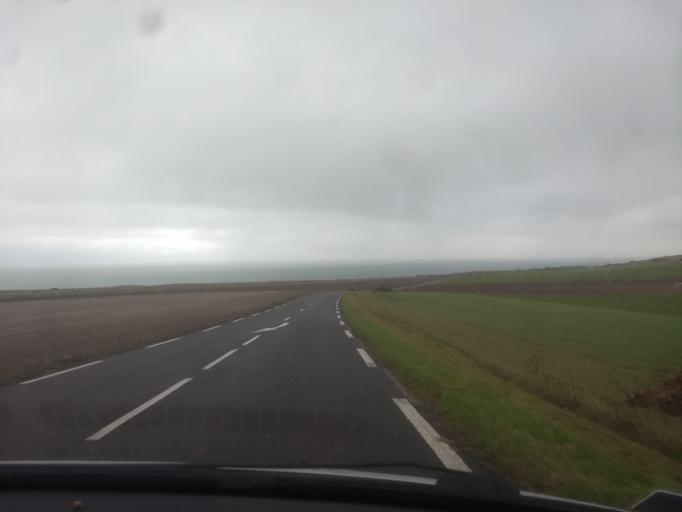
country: FR
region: Nord-Pas-de-Calais
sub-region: Departement du Pas-de-Calais
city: Sangatte
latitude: 50.9314
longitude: 1.7220
